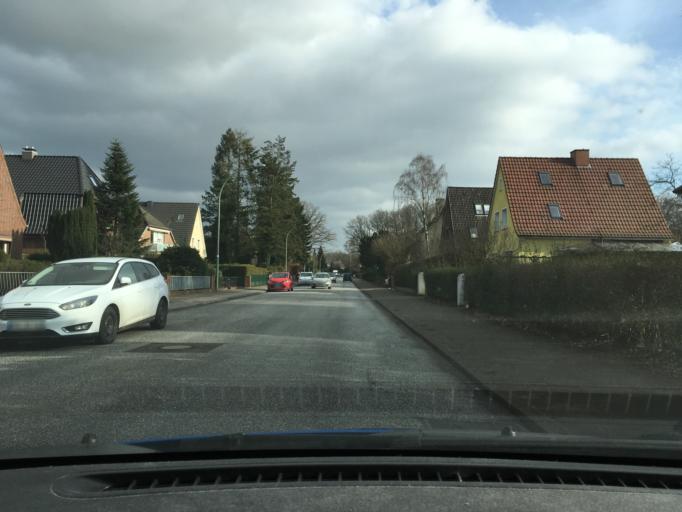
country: DE
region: Schleswig-Holstein
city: Wedel
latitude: 53.5751
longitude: 9.7146
